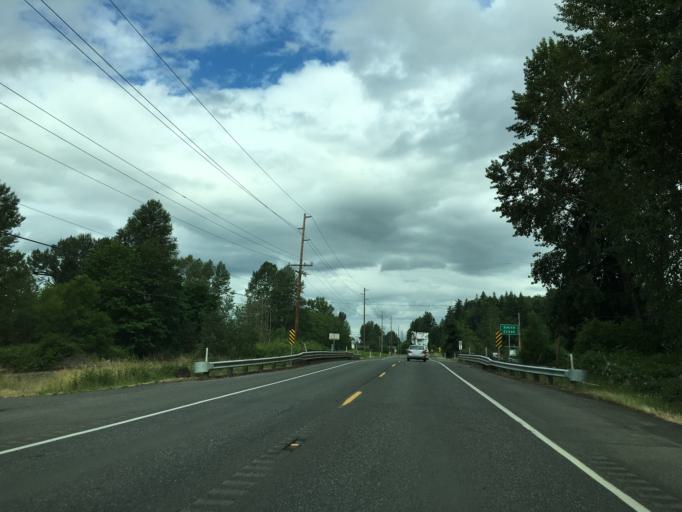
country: US
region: Washington
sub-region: Whatcom County
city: Nooksack
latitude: 48.8412
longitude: -122.2600
